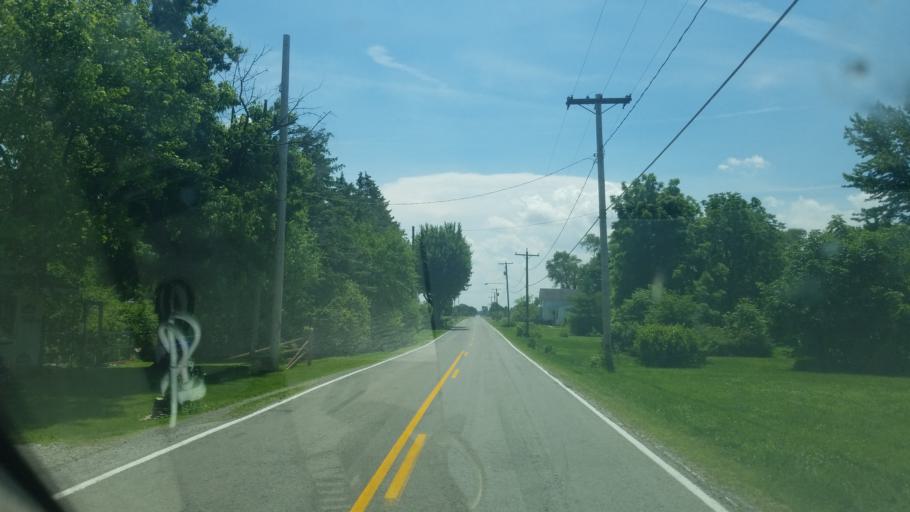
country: US
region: Ohio
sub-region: Hancock County
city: Arlington
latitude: 40.9337
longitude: -83.5945
